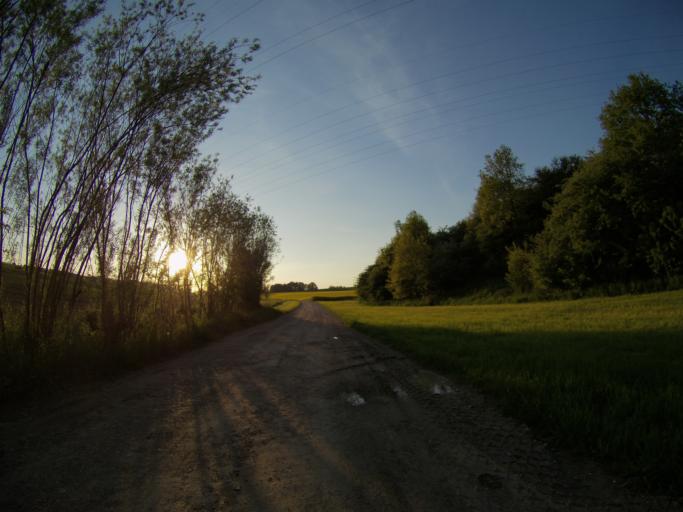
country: DE
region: Bavaria
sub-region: Upper Bavaria
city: Marzling
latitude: 48.4163
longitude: 11.7828
